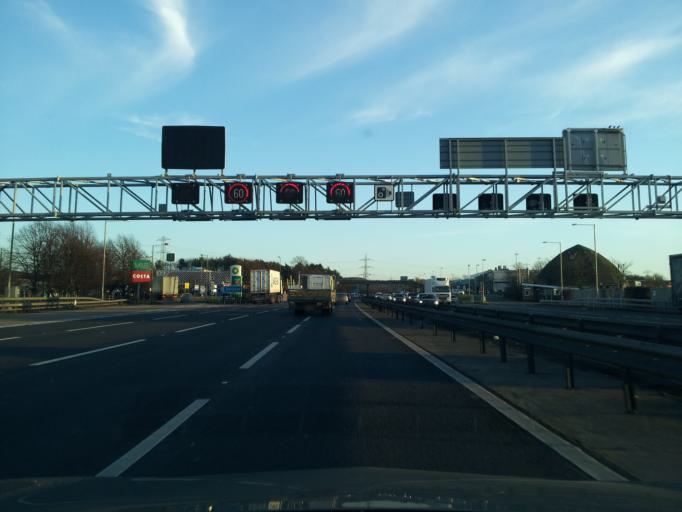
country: GB
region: England
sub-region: Central Bedfordshire
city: Harlington
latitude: 51.9494
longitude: -0.5041
